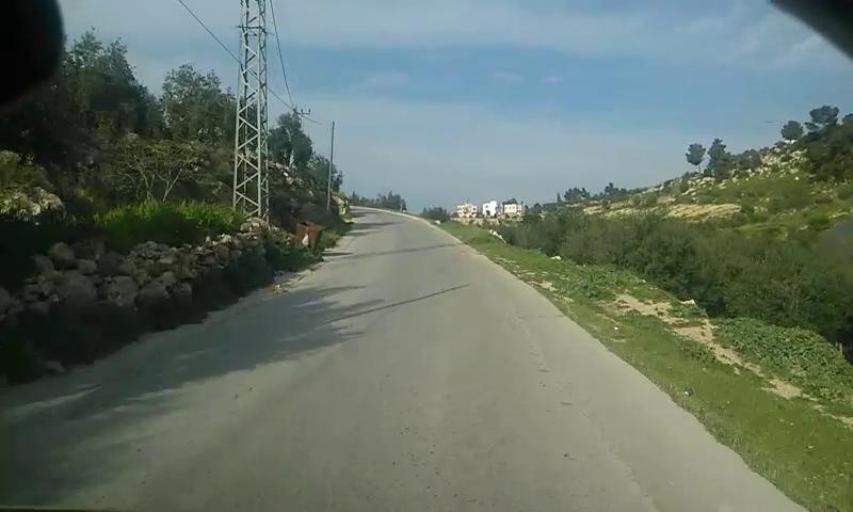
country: PS
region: West Bank
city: Bayt Ula
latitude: 31.5844
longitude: 35.0230
